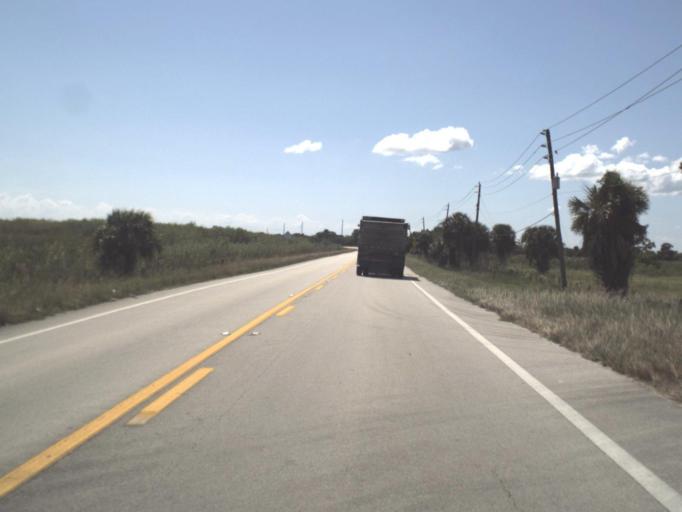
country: US
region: Florida
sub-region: Okeechobee County
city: Okeechobee
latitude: 27.1925
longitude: -80.8481
